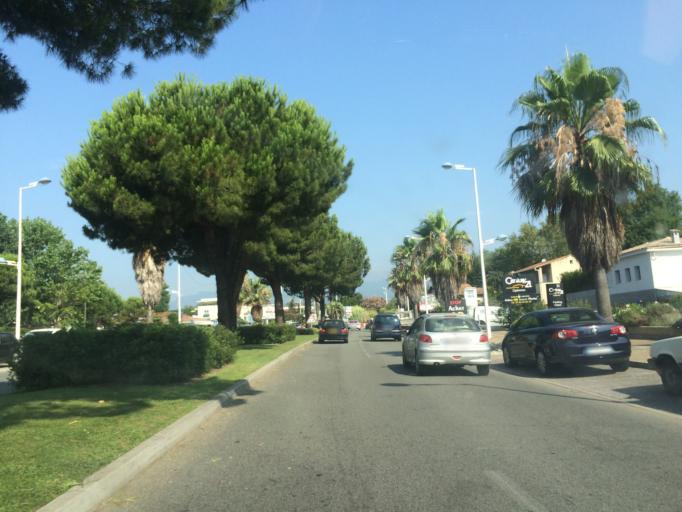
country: FR
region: Provence-Alpes-Cote d'Azur
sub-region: Departement des Alpes-Maritimes
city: Villeneuve-Loubet
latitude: 43.6616
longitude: 7.1331
